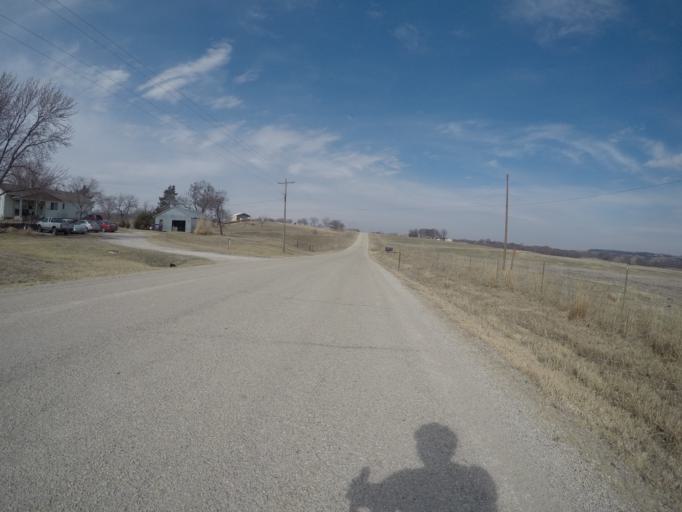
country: US
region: Kansas
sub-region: Geary County
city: Grandview Plaza
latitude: 39.0473
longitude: -96.7431
